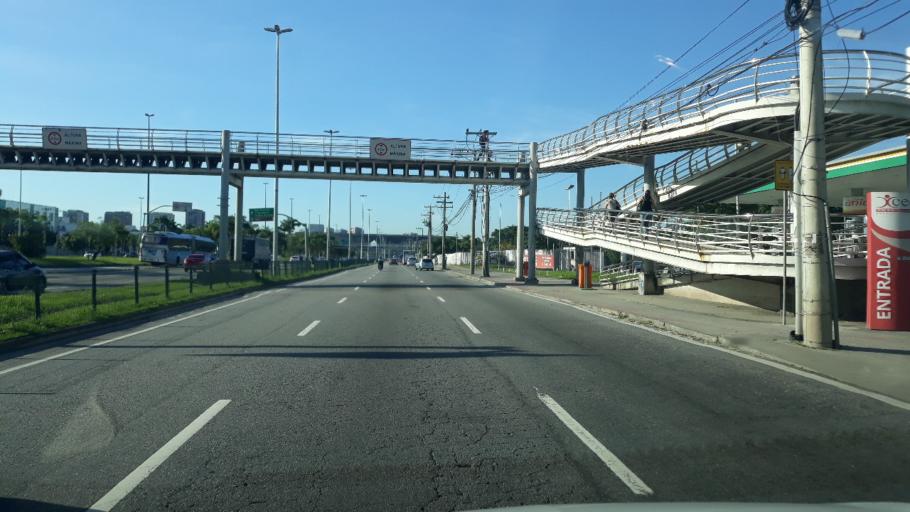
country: BR
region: Rio de Janeiro
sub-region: Rio De Janeiro
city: Rio de Janeiro
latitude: -22.9893
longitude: -43.3661
